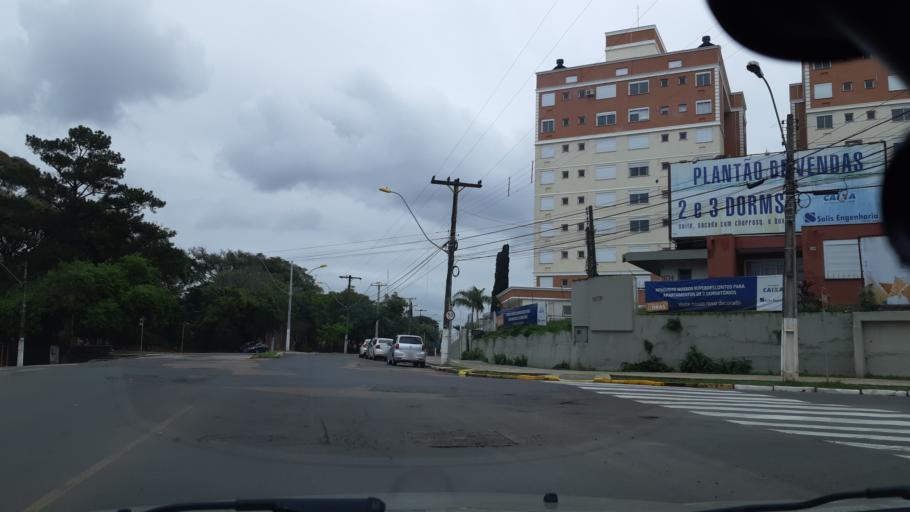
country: BR
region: Rio Grande do Sul
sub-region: Sapucaia Do Sul
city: Sapucaia
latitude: -29.8492
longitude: -51.1585
